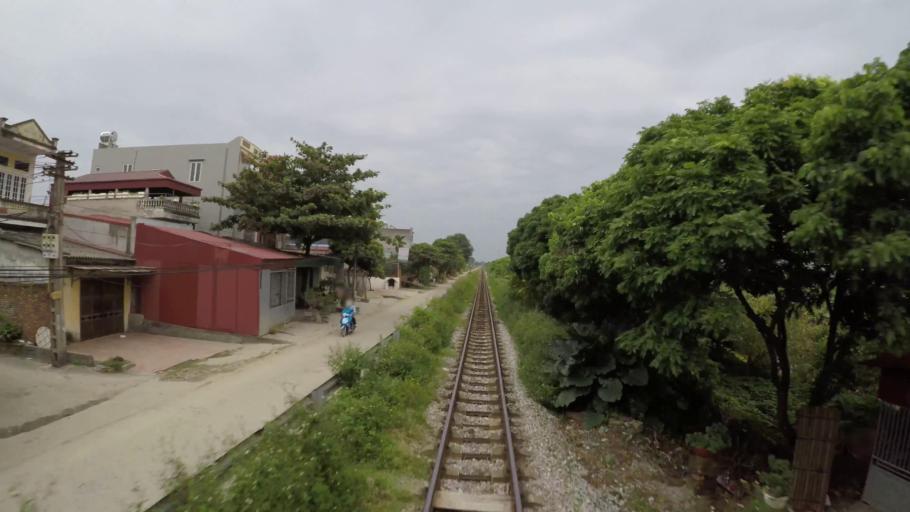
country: VN
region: Hai Duong
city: Lai Cach
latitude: 20.9516
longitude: 106.2357
